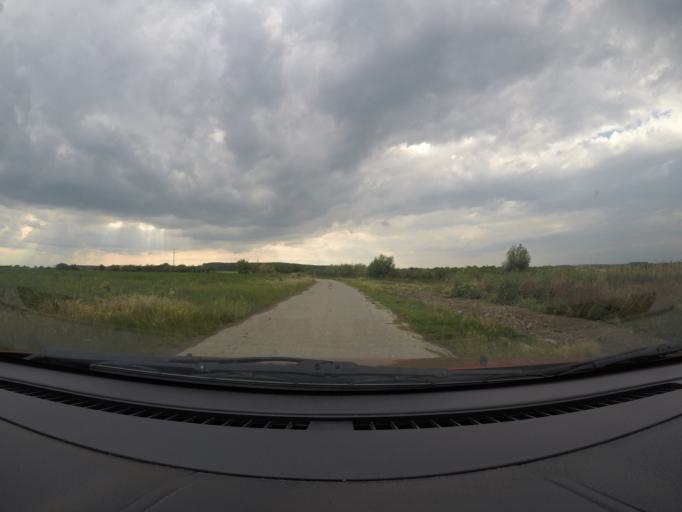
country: RS
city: Uzdin
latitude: 45.2044
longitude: 20.6051
